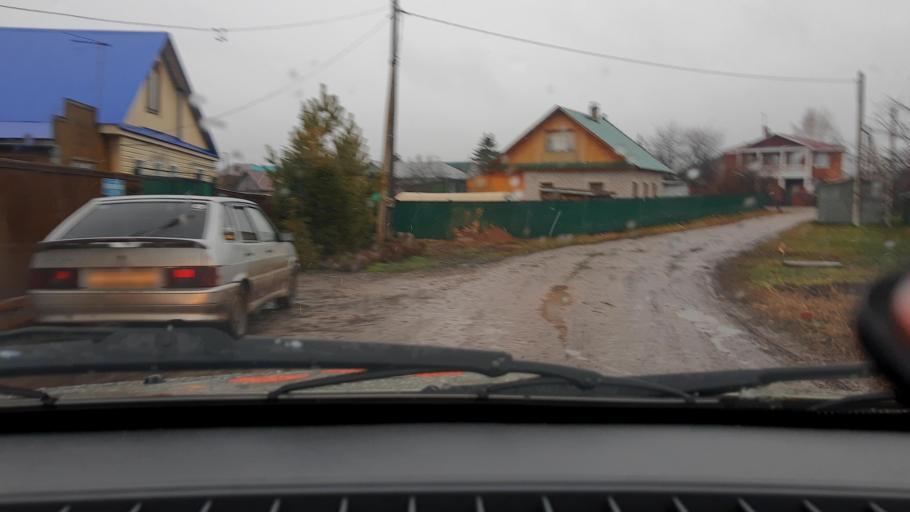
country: RU
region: Bashkortostan
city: Ufa
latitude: 54.6142
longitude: 55.9399
